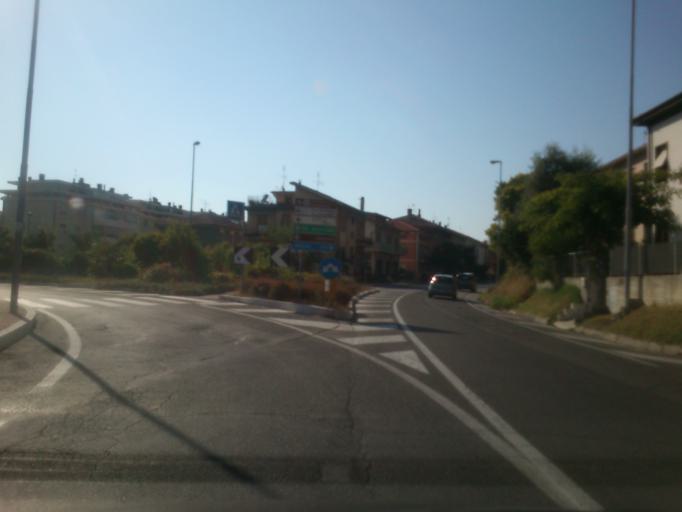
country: IT
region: The Marches
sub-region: Provincia di Pesaro e Urbino
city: Pesaro
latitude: 43.9110
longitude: 12.8745
